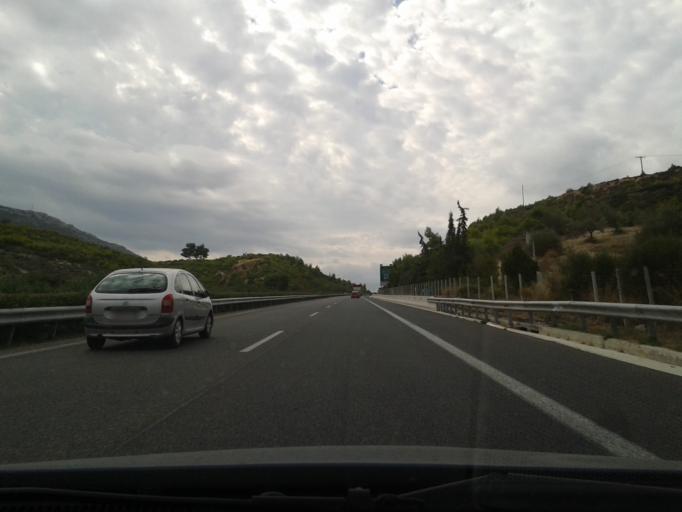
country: GR
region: Peloponnese
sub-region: Nomos Korinthias
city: Arkhaia Korinthos
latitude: 37.8673
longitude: 22.8508
